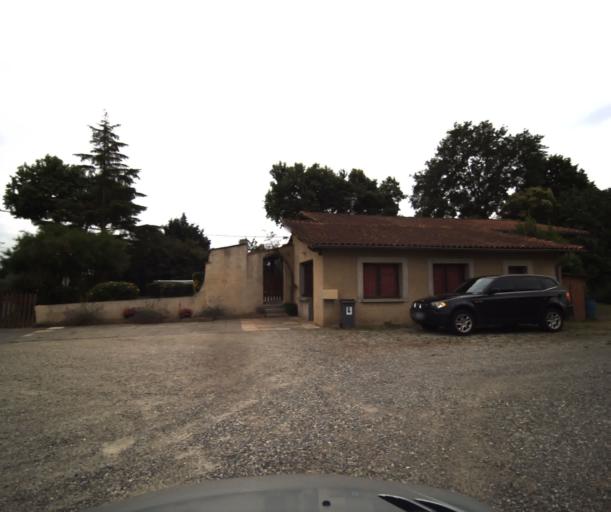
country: FR
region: Midi-Pyrenees
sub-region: Departement de la Haute-Garonne
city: Labarthe-sur-Leze
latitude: 43.4561
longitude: 1.3879
